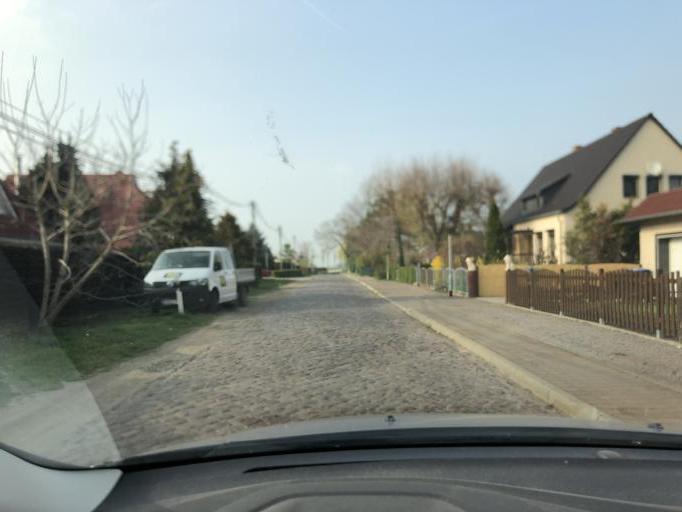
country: DE
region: Saxony-Anhalt
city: Zorbig
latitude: 51.6028
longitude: 12.1112
